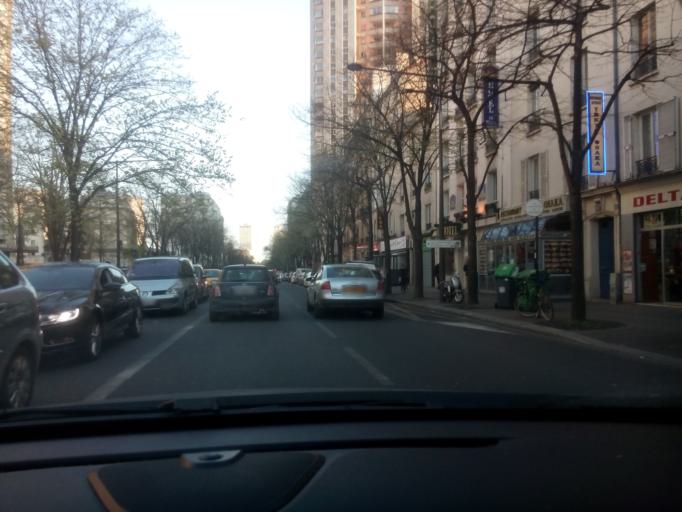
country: FR
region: Ile-de-France
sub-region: Departement du Val-de-Marne
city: Le Kremlin-Bicetre
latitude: 48.8304
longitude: 2.3565
